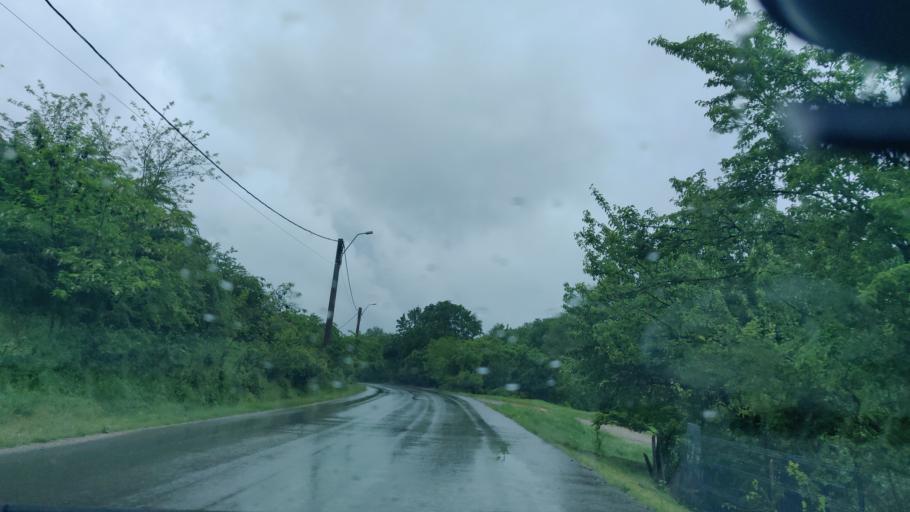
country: RO
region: Giurgiu
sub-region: Comuna Bulbucata
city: Bulbucata
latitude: 44.2885
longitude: 25.7950
